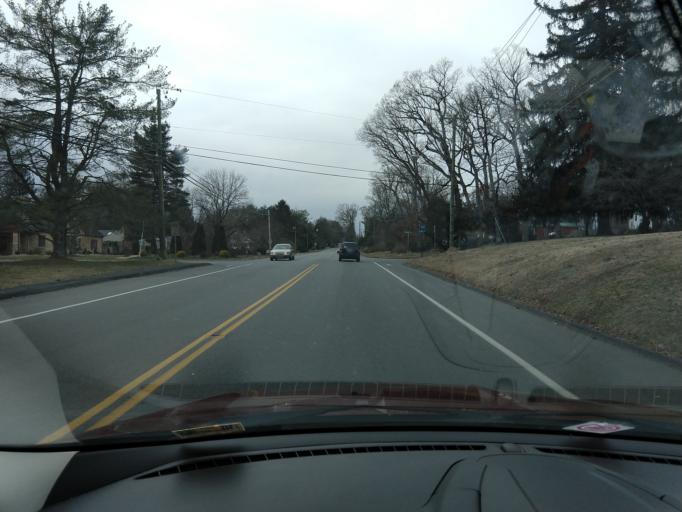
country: US
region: Virginia
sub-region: City of Waynesboro
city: Waynesboro
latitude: 38.0700
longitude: -78.9132
